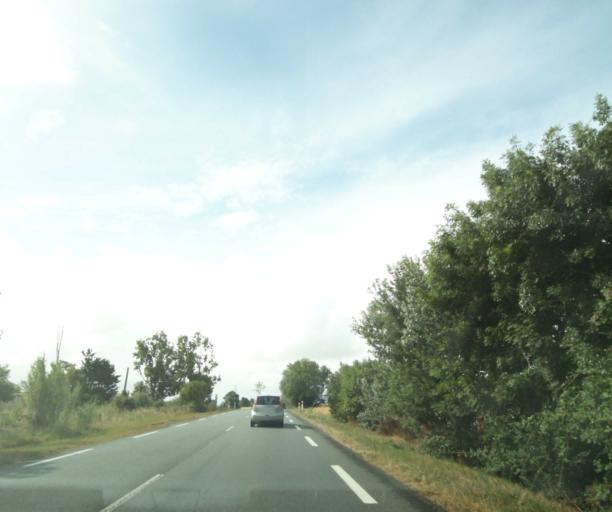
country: FR
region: Poitou-Charentes
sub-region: Departement de la Charente-Maritime
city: Charron
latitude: 46.2915
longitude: -1.0842
